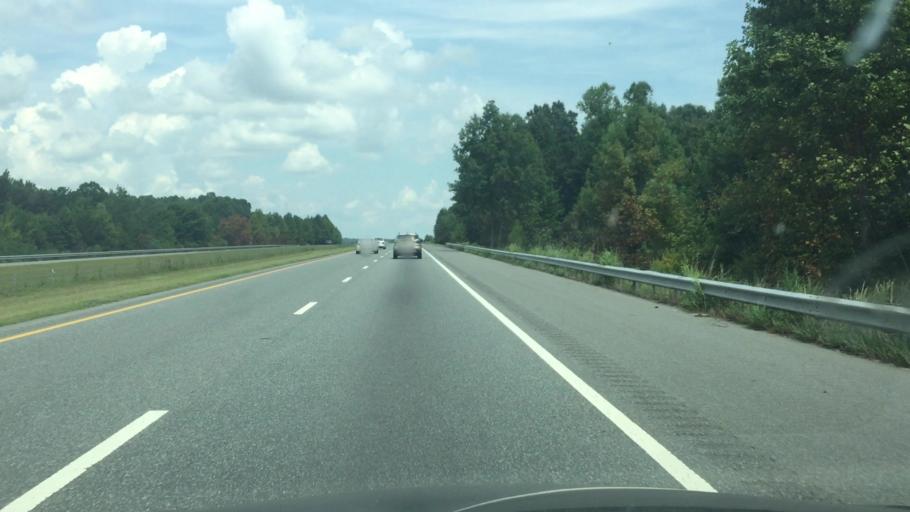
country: US
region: North Carolina
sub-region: Montgomery County
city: Biscoe
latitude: 35.4798
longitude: -79.7822
